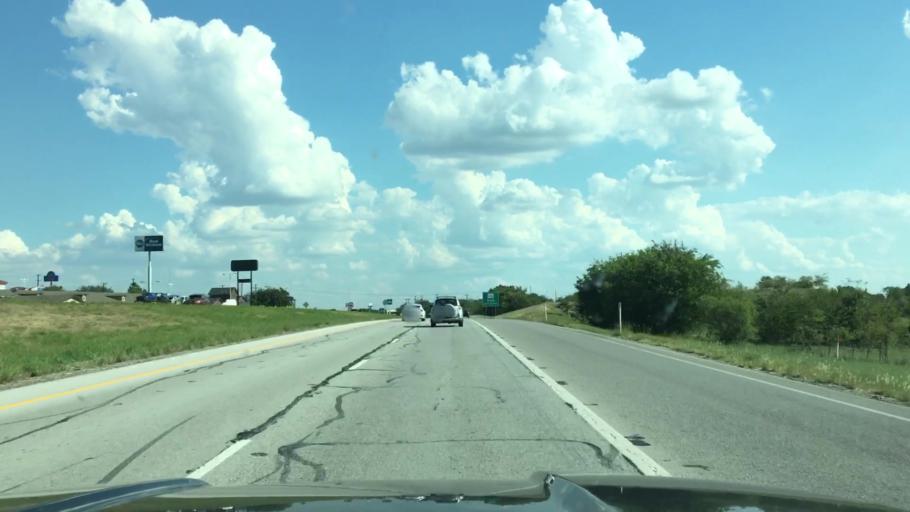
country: US
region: Texas
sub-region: Wise County
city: Decatur
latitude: 33.2208
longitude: -97.5896
